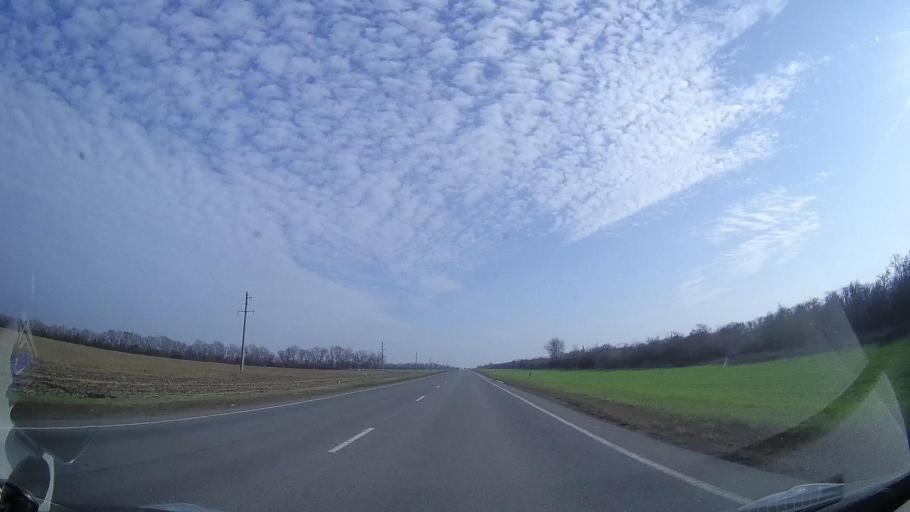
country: RU
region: Rostov
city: Gigant
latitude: 46.5255
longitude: 41.2388
